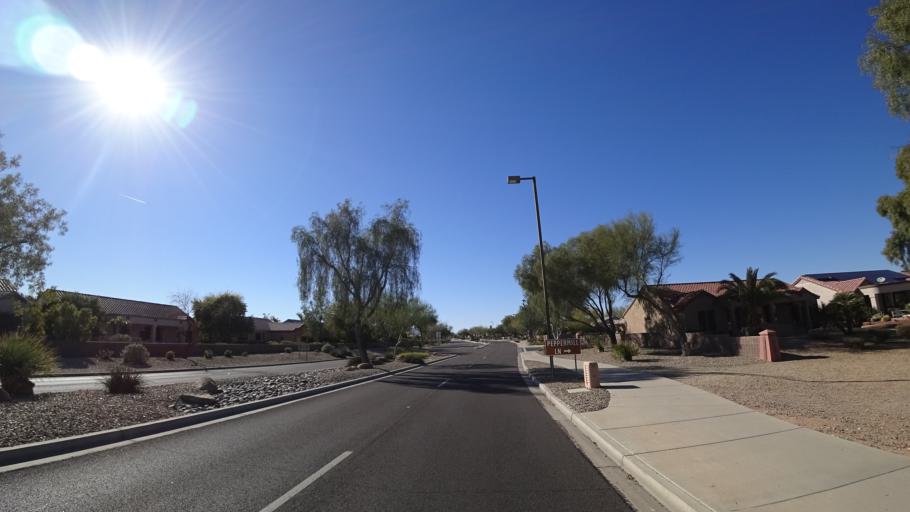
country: US
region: Arizona
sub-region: Maricopa County
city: Sun City West
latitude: 33.6458
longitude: -112.4045
